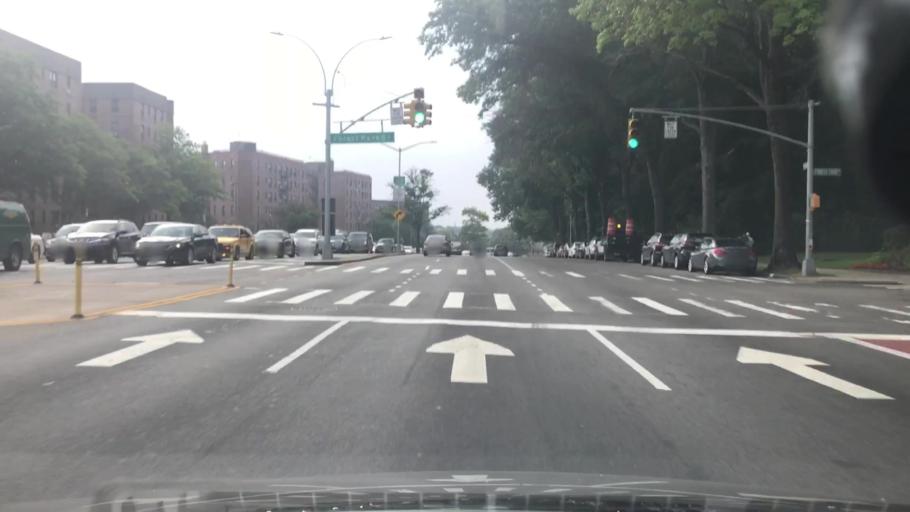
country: US
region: New York
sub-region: Queens County
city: Borough of Queens
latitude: 40.7007
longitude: -73.8548
